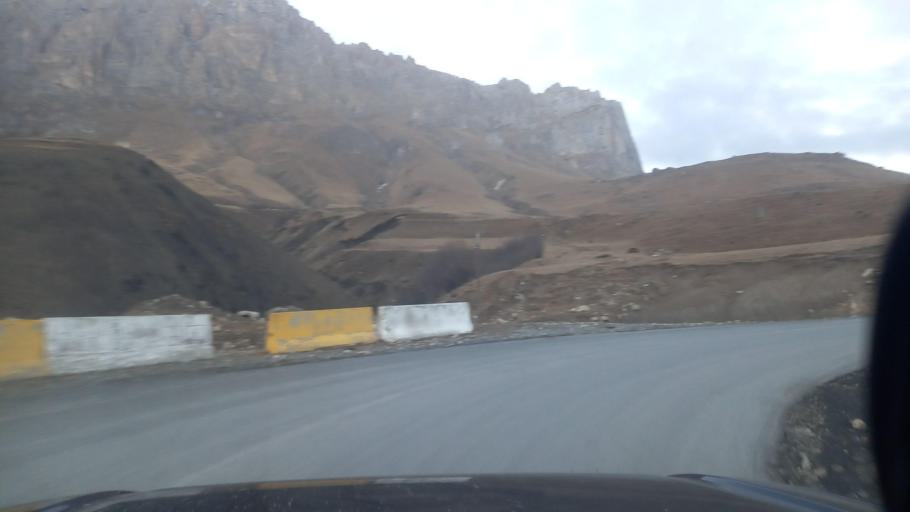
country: RU
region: Ingushetiya
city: Dzhayrakh
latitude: 42.8220
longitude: 44.8203
